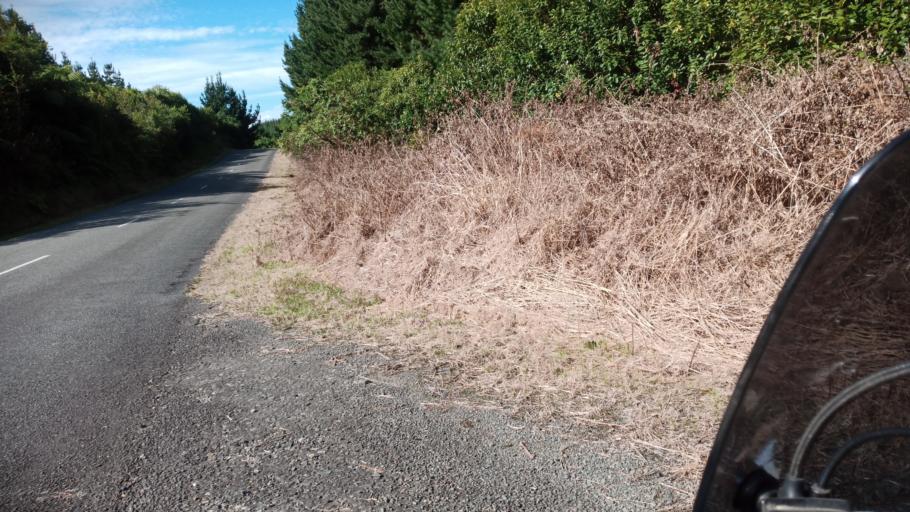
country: NZ
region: Hawke's Bay
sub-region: Wairoa District
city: Wairoa
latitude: -39.0030
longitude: 177.0854
